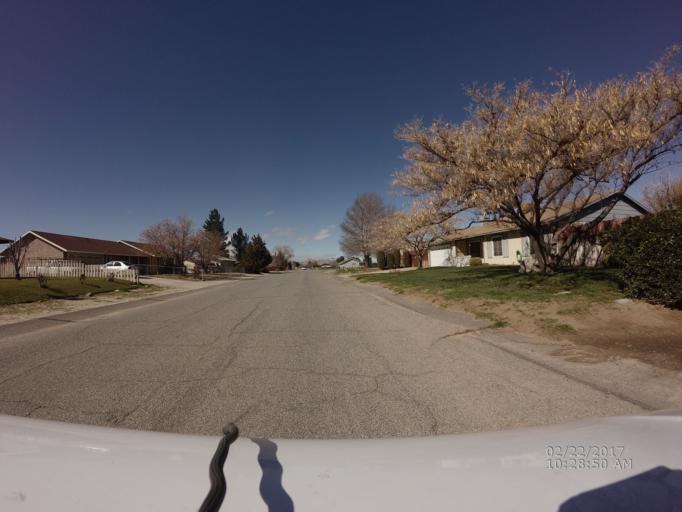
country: US
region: California
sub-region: Los Angeles County
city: Lake Los Angeles
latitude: 34.6303
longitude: -117.8219
